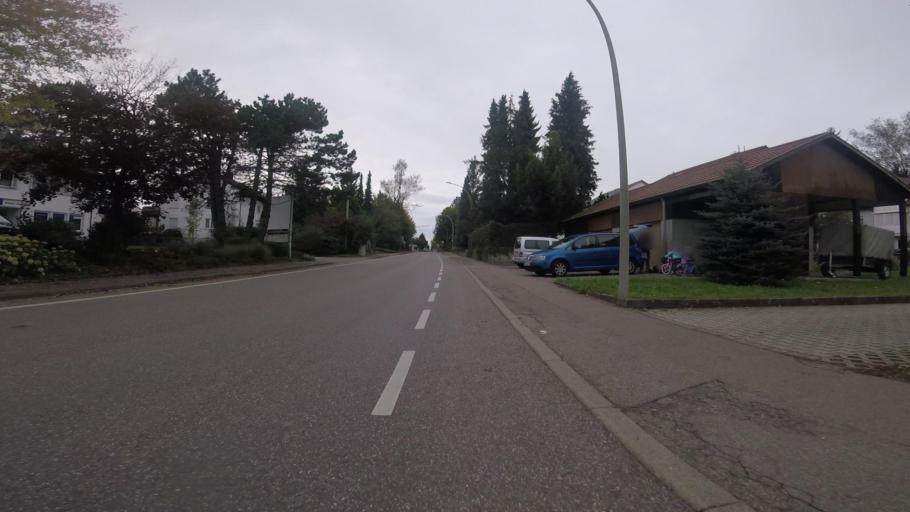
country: DE
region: Baden-Wuerttemberg
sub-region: Regierungsbezirk Stuttgart
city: Backnang
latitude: 48.9379
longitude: 9.4454
